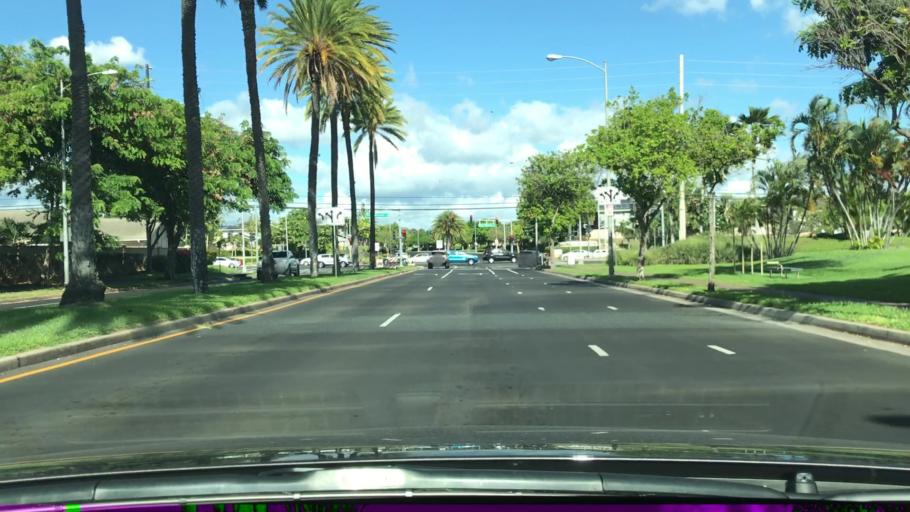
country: US
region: Hawaii
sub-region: Honolulu County
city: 'Ewa Gentry
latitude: 21.3412
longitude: -158.0262
